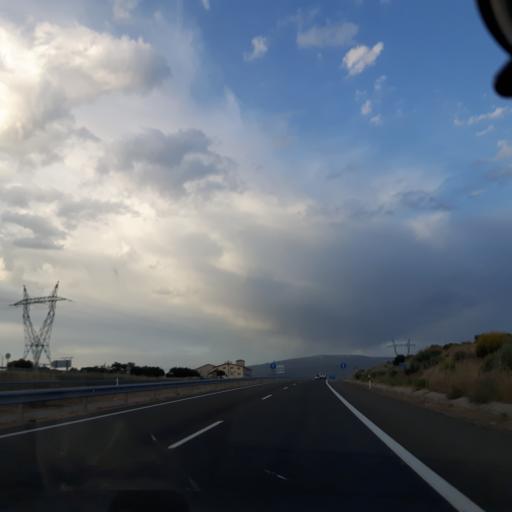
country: ES
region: Castille and Leon
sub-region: Provincia de Salamanca
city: Fuentes de Bejar
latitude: 40.4975
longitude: -5.6758
